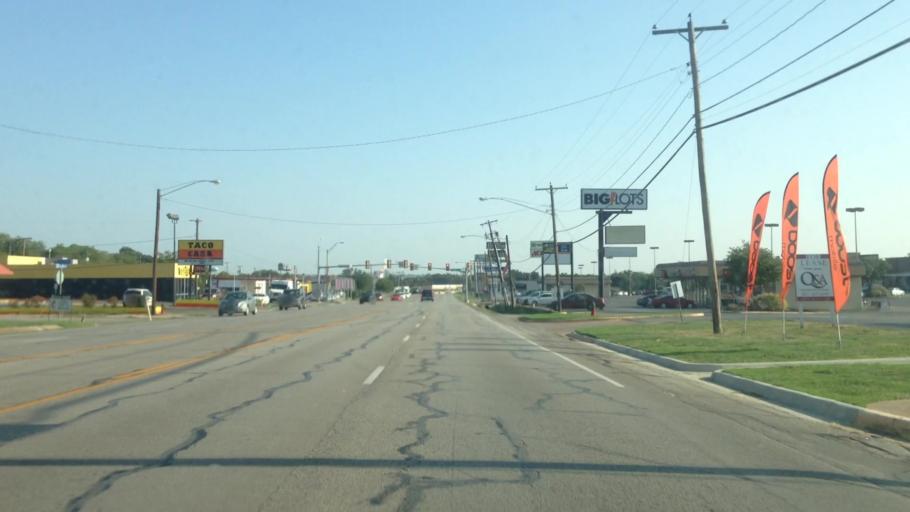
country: US
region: Texas
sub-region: Tarrant County
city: Haltom City
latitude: 32.8067
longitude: -97.2646
